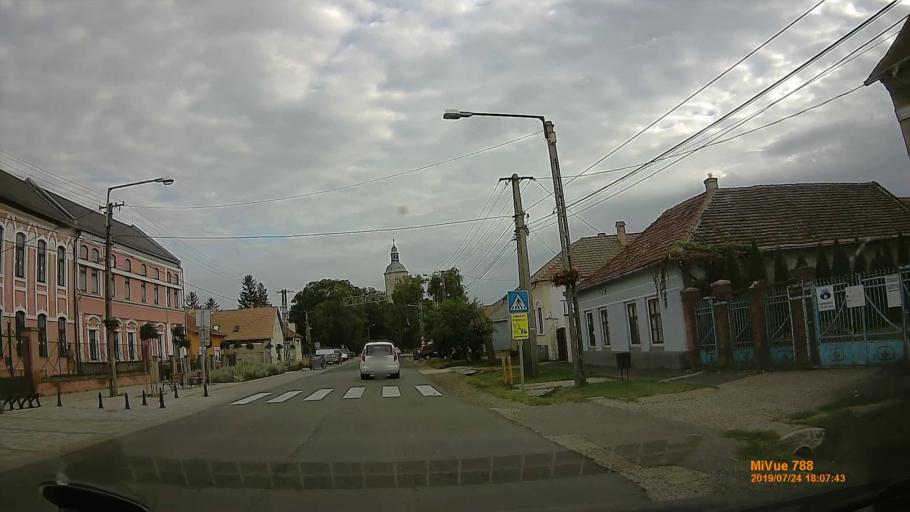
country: HU
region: Borsod-Abauj-Zemplen
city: Abaujszanto
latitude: 48.2781
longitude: 21.1862
